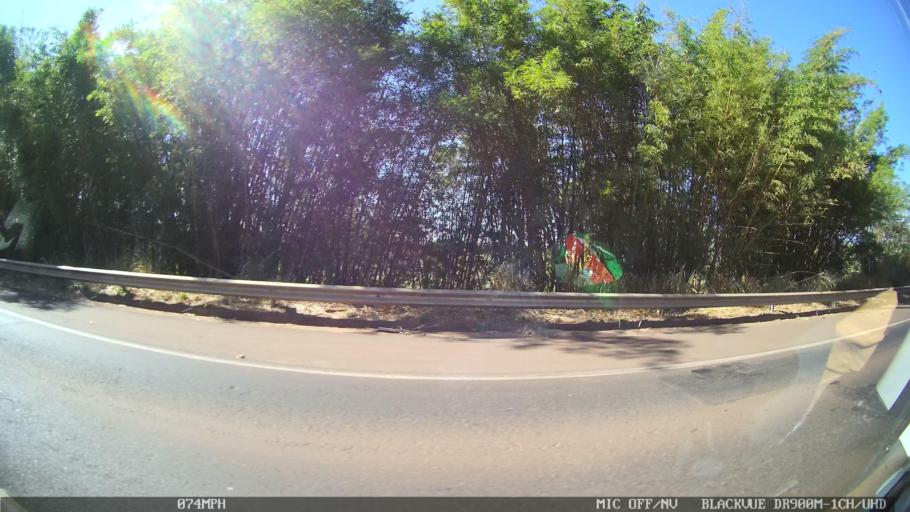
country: BR
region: Sao Paulo
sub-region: Olimpia
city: Olimpia
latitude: -20.7190
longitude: -48.8716
